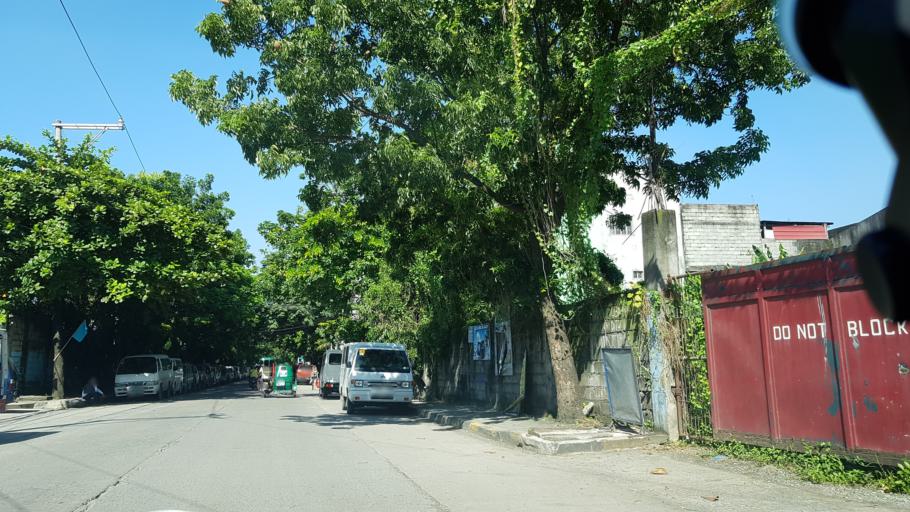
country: PH
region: Calabarzon
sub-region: Province of Rizal
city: Cainta
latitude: 14.5713
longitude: 121.0965
